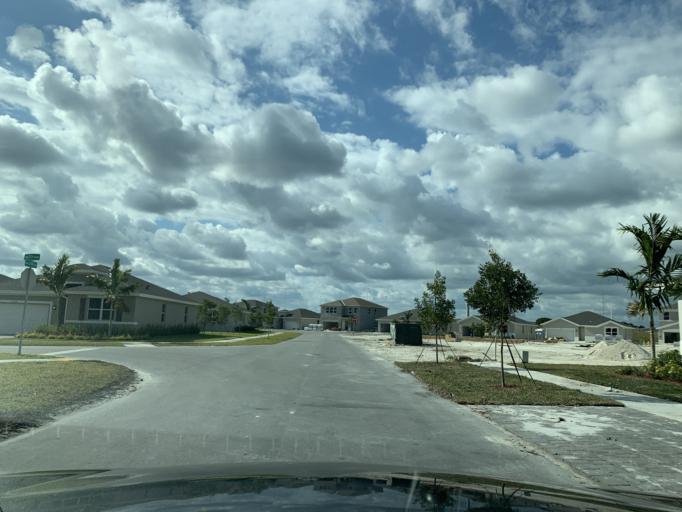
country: US
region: Florida
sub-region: Miami-Dade County
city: Naranja
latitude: 25.5120
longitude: -80.4080
